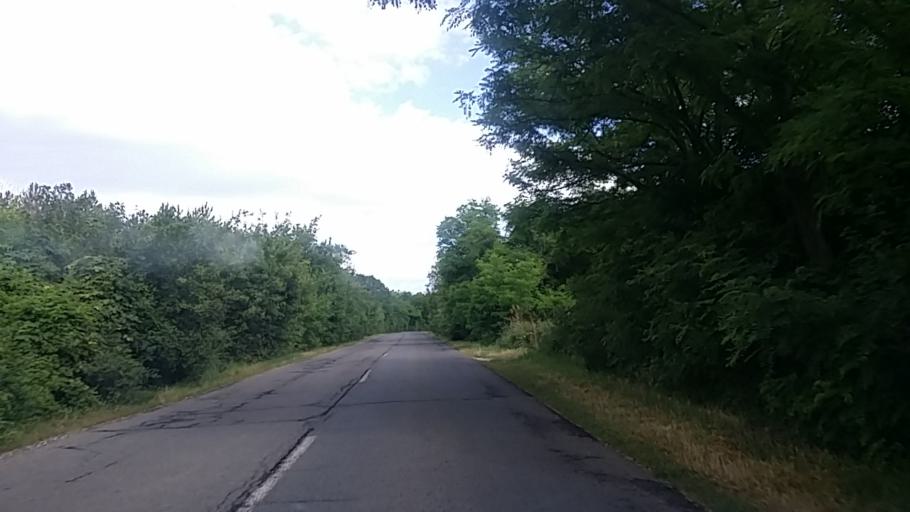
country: HU
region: Pest
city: Kosd
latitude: 47.8135
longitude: 19.2406
